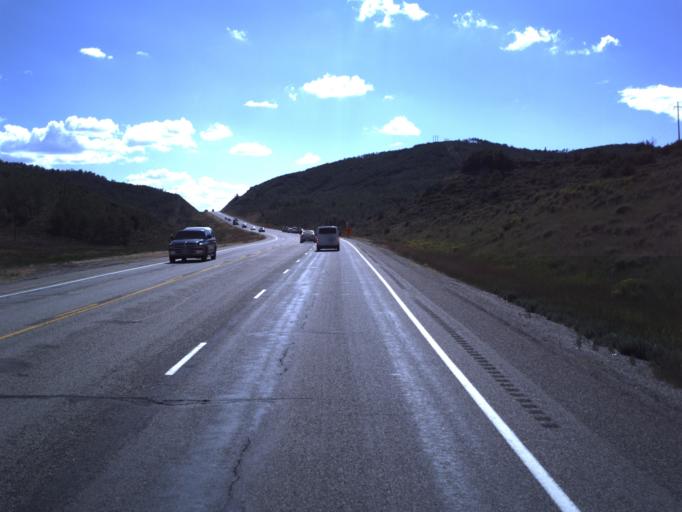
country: US
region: Utah
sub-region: Summit County
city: Francis
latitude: 40.1938
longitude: -111.0096
